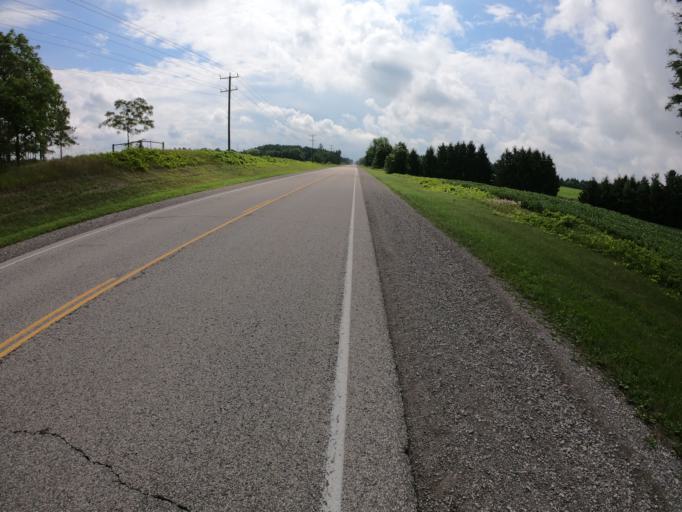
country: CA
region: Ontario
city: Waterloo
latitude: 43.4515
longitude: -80.6474
